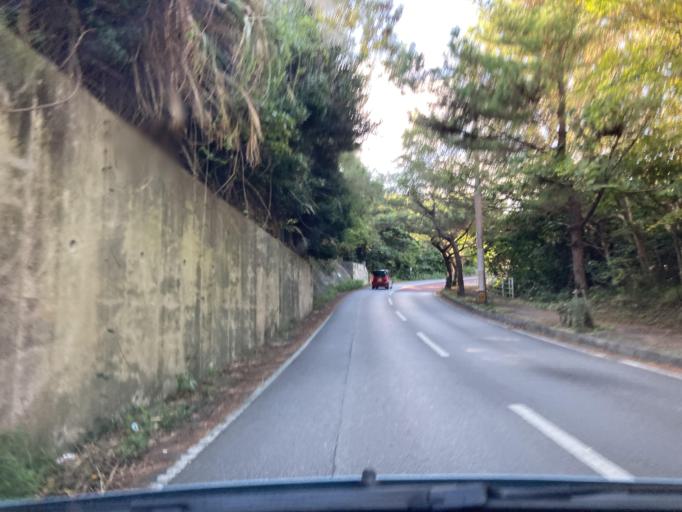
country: JP
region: Okinawa
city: Ginowan
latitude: 26.2164
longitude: 127.7509
